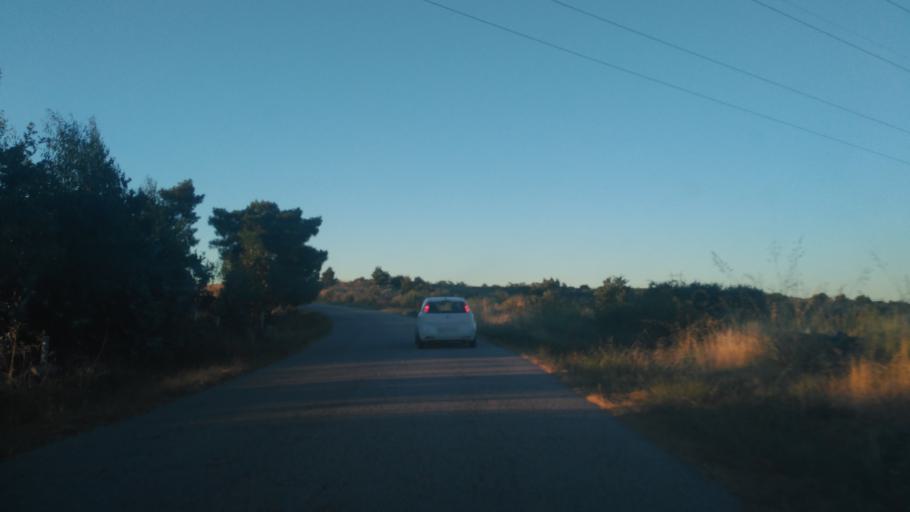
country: ES
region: Castille and Leon
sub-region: Provincia de Salamanca
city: Aldeadavila de la Ribera
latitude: 41.2035
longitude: -6.6437
